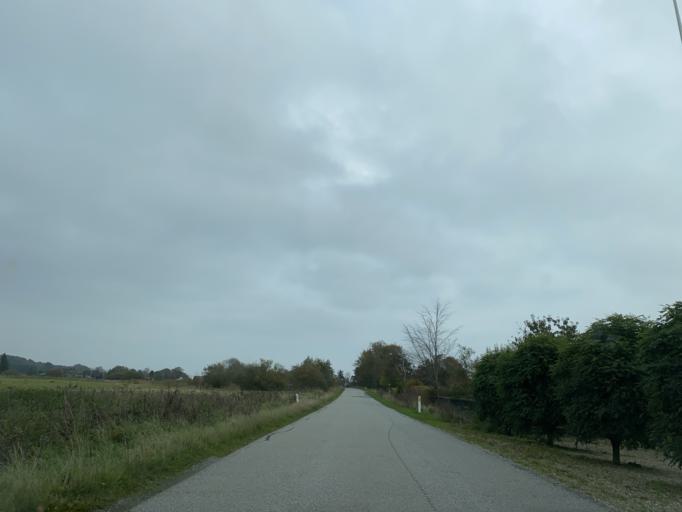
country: DK
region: South Denmark
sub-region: Aabenraa Kommune
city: Lojt Kirkeby
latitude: 55.1572
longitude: 9.4901
